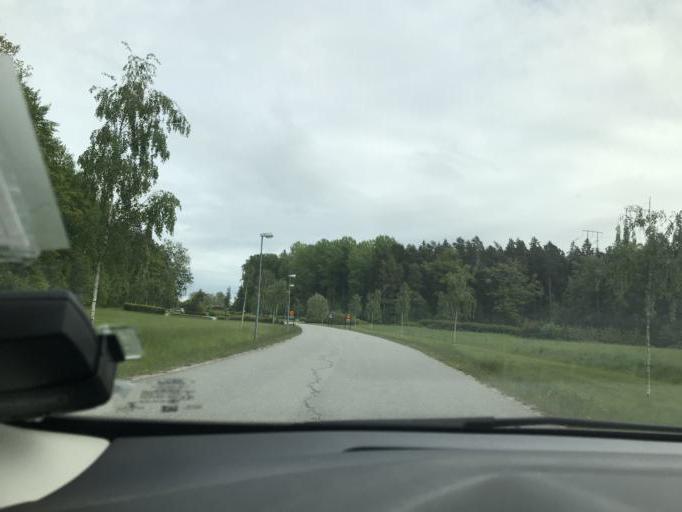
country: SE
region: Stockholm
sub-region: Botkyrka Kommun
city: Alby
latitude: 59.2187
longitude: 17.8453
